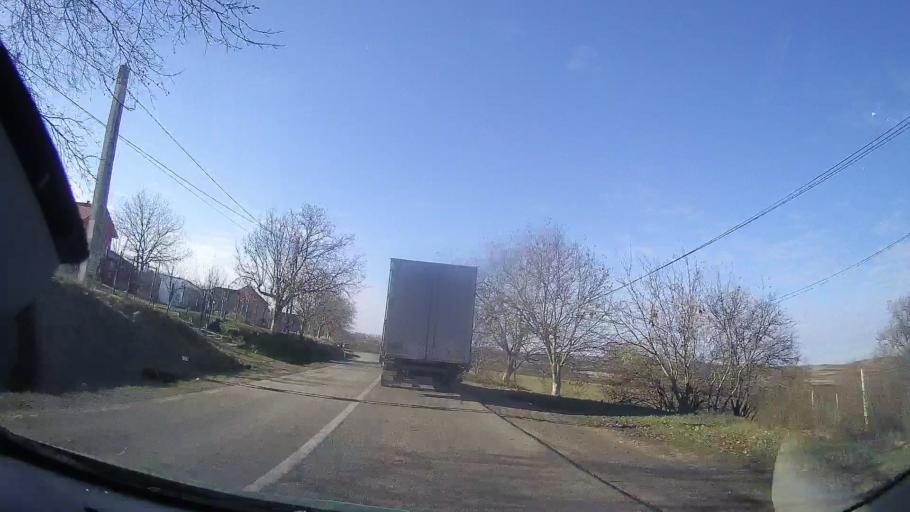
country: RO
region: Cluj
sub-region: Comuna Mociu
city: Mociu
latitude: 46.7975
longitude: 24.0167
